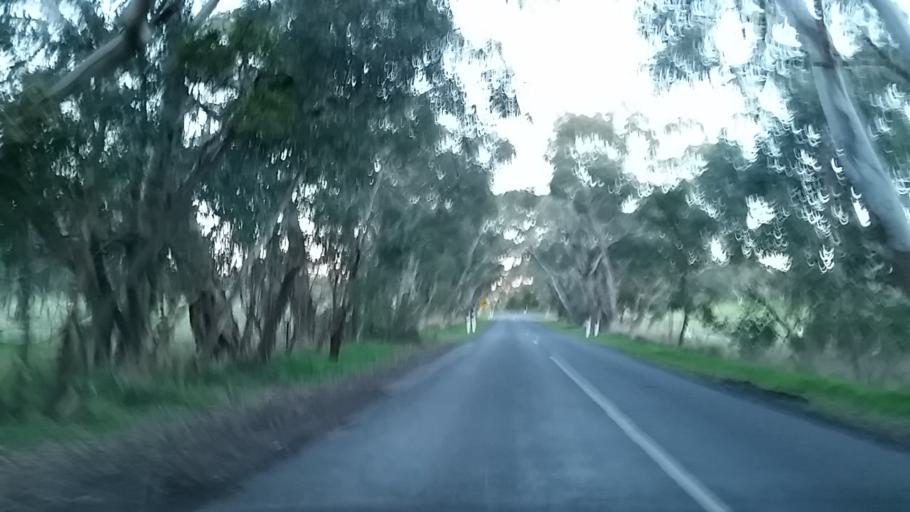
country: AU
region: South Australia
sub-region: Alexandrina
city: Mount Compass
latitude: -35.2889
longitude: 138.6073
